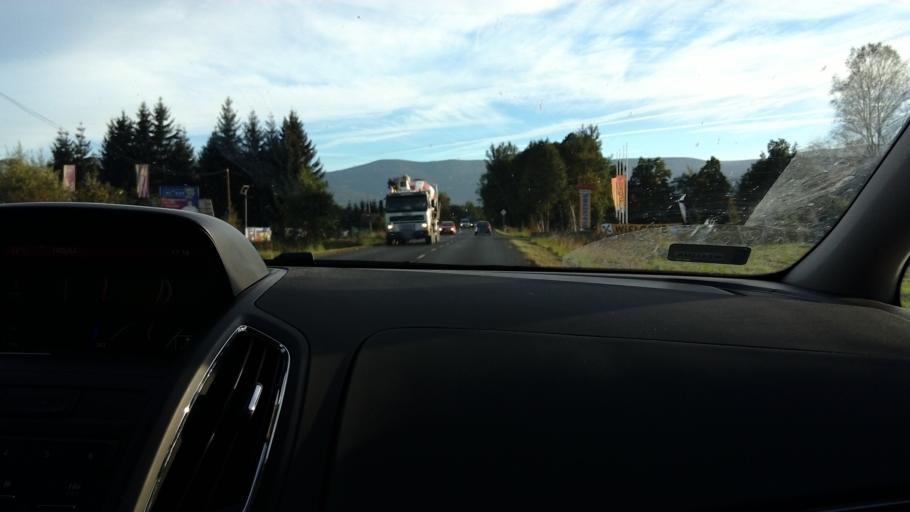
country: PL
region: Lower Silesian Voivodeship
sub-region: Powiat jeleniogorski
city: Myslakowice
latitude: 50.8392
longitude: 15.7746
